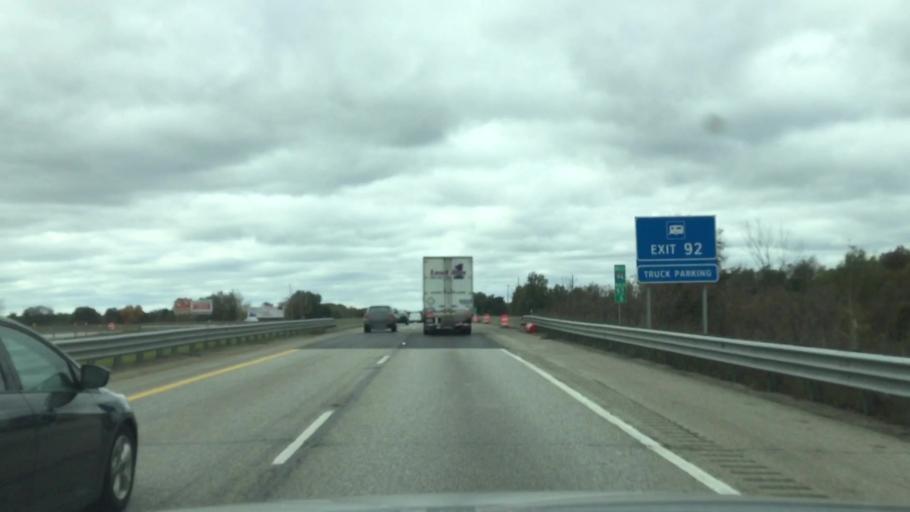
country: US
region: Michigan
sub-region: Calhoun County
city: Springfield
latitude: 42.2709
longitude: -85.2859
